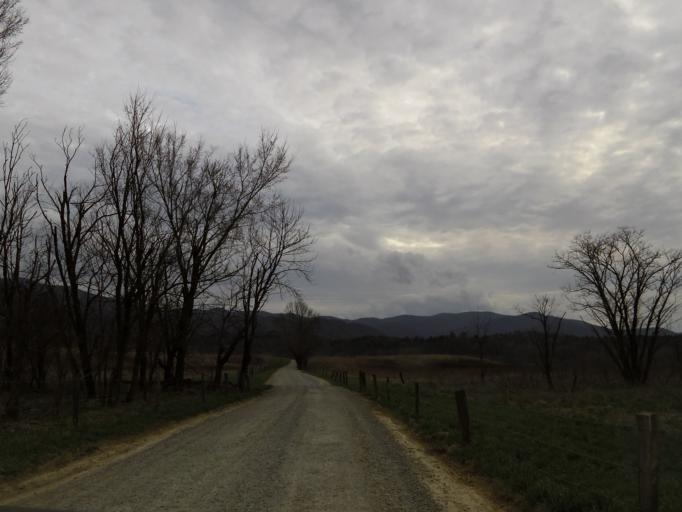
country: US
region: Tennessee
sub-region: Blount County
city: Wildwood
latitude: 35.5993
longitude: -83.8240
